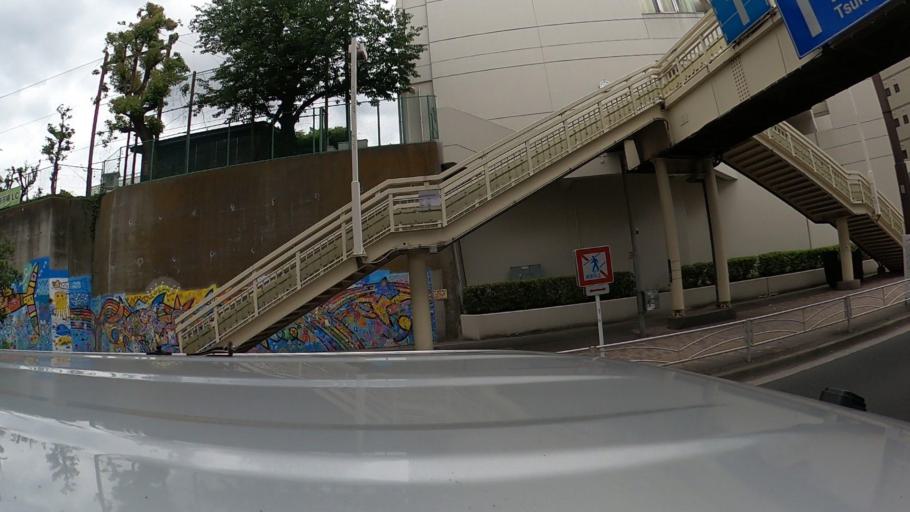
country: JP
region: Kanagawa
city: Yokohama
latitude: 35.4713
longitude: 139.6312
